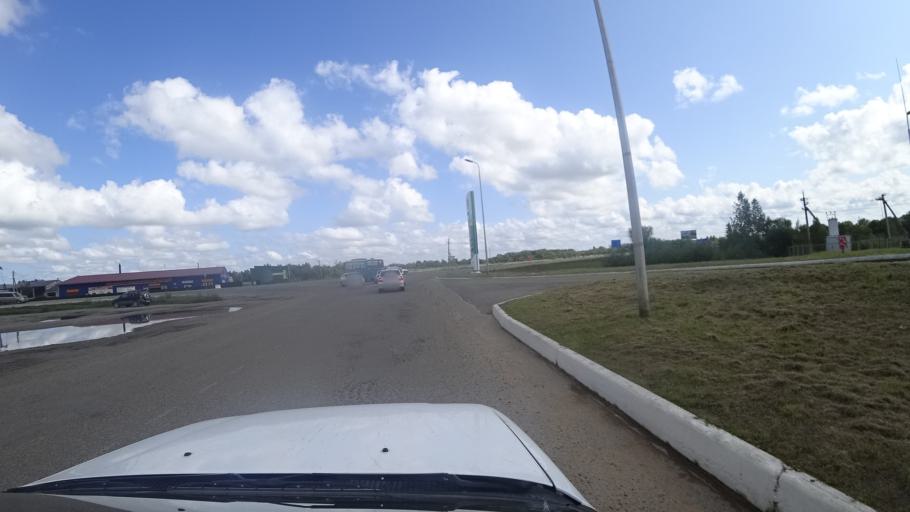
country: RU
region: Primorskiy
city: Dal'nerechensk
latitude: 45.9243
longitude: 133.7729
